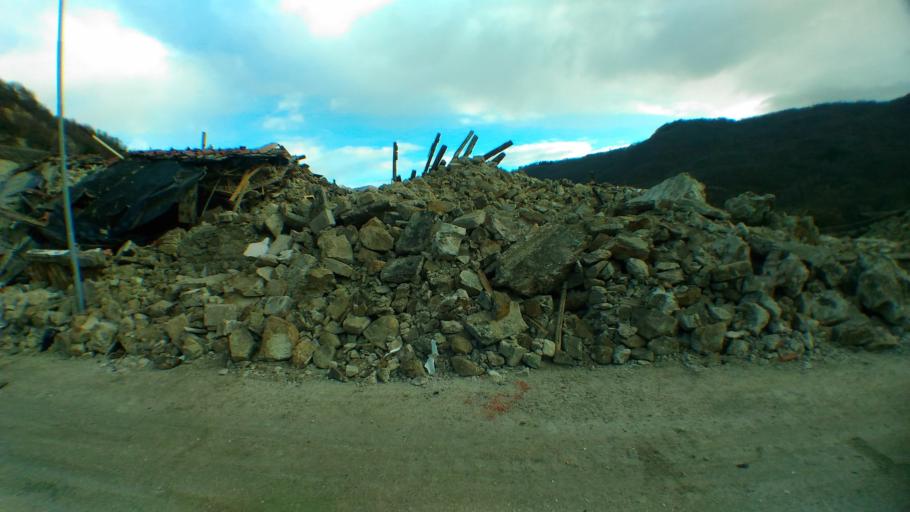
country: IT
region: The Marches
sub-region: Provincia di Ascoli Piceno
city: Arquata del Tronto
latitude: 42.7509
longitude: 13.2703
